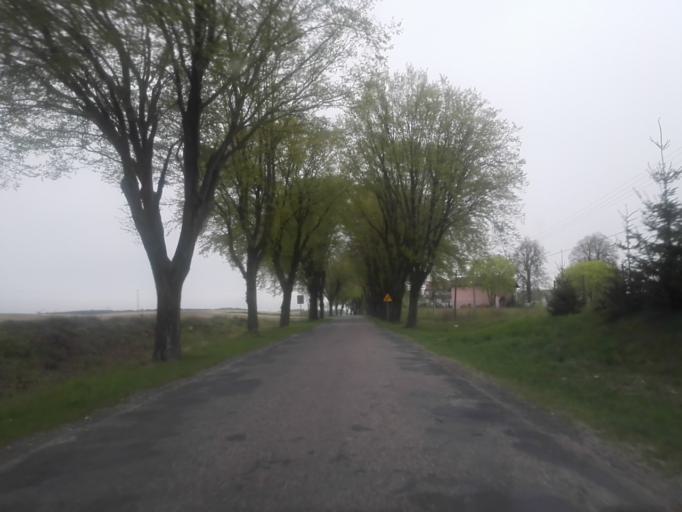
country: PL
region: Kujawsko-Pomorskie
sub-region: Powiat brodnicki
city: Gorzno
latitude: 53.2069
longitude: 19.6368
